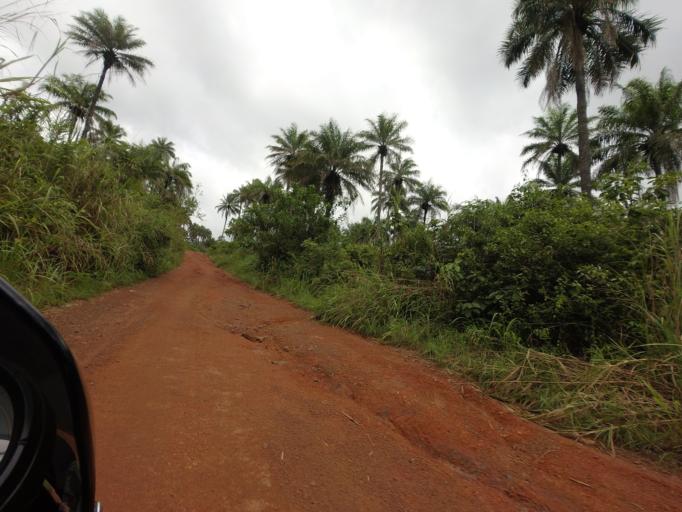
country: SL
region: Northern Province
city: Kambia
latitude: 9.1034
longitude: -12.9888
